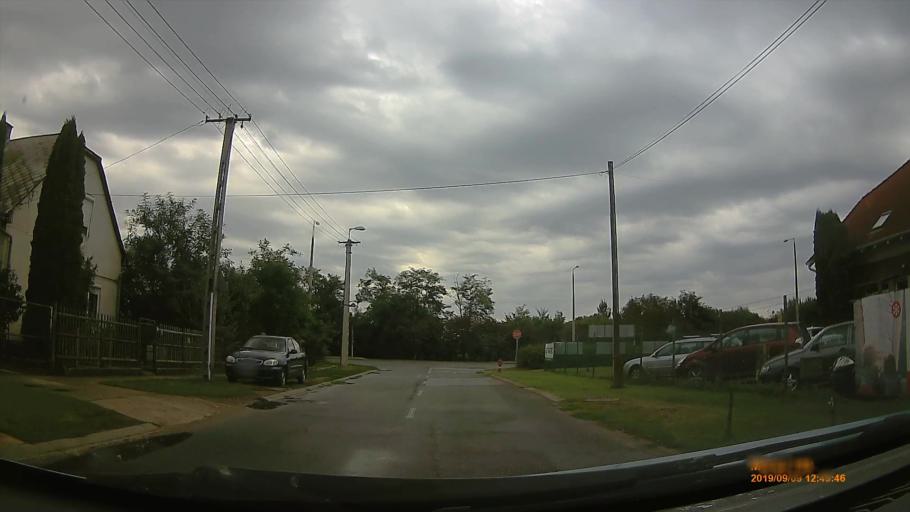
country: HU
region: Szabolcs-Szatmar-Bereg
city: Nyirpazony
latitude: 47.9489
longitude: 21.7831
